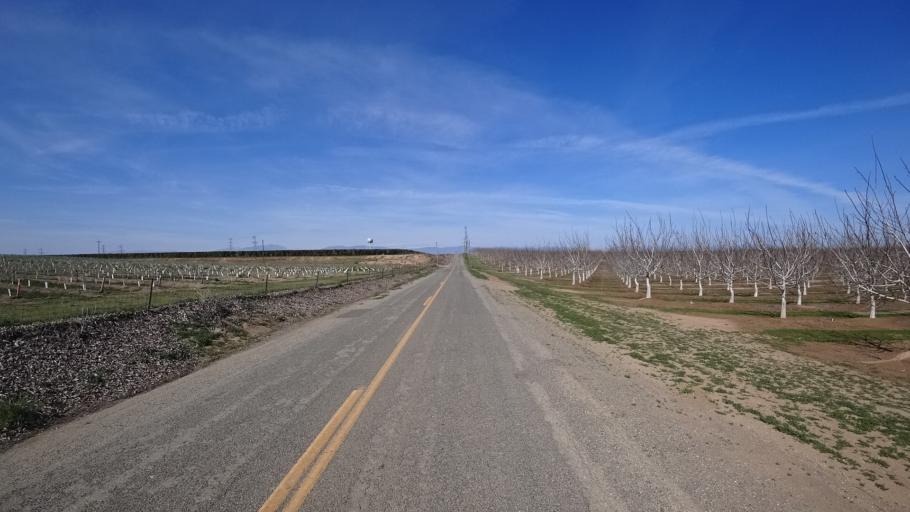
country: US
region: California
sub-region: Glenn County
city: Willows
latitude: 39.6116
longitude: -122.2671
